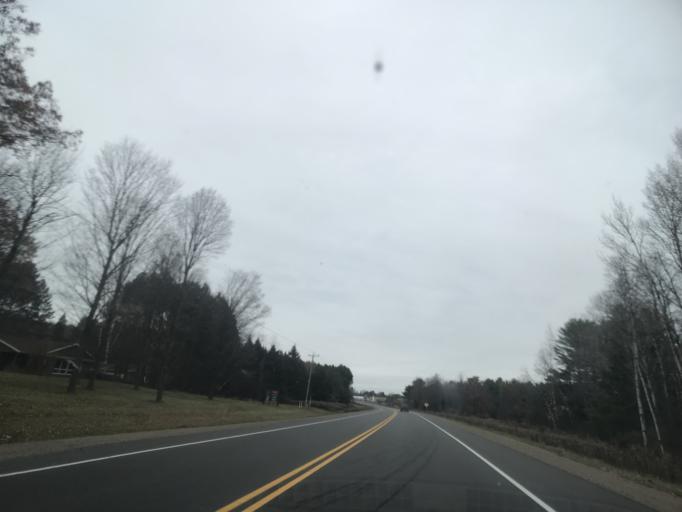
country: US
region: Wisconsin
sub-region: Menominee County
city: Legend Lake
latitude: 45.2948
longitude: -88.5133
